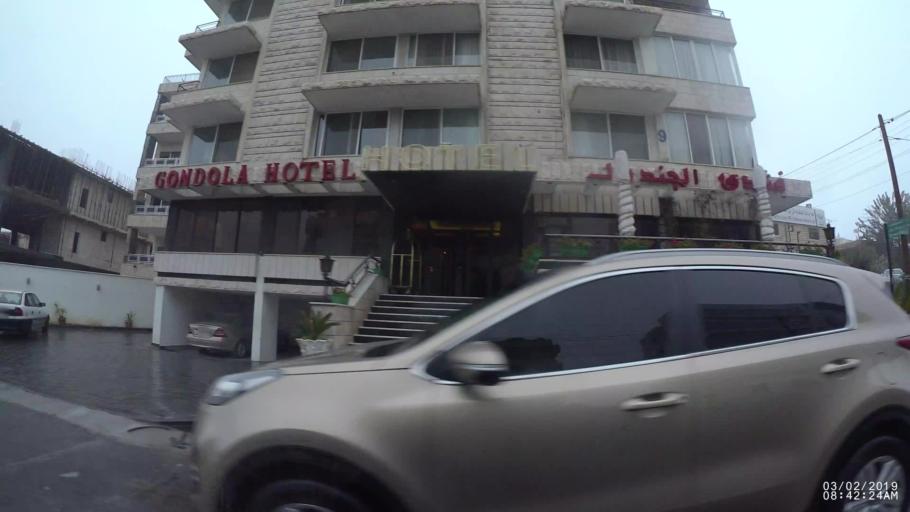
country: JO
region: Amman
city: Wadi as Sir
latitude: 31.9625
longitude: 35.8782
